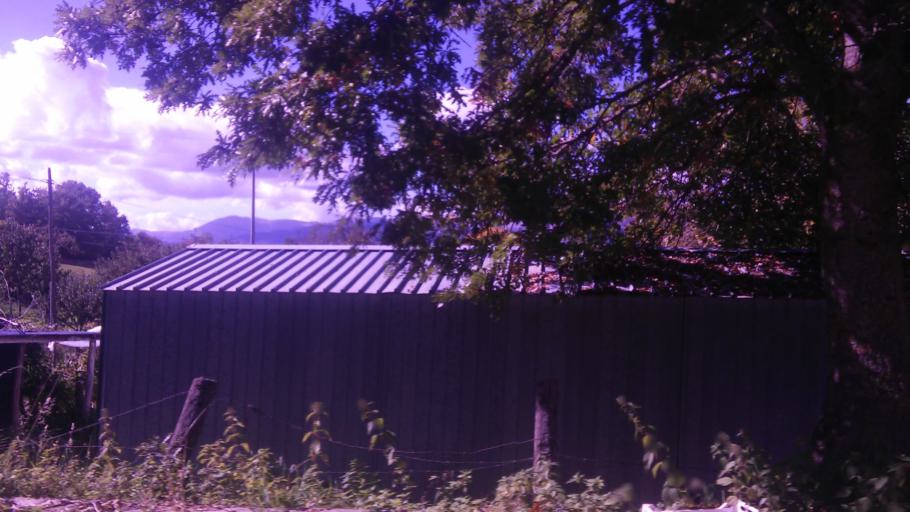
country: IT
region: Latium
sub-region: Provincia di Rieti
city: Amatrice
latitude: 42.6314
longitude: 13.3250
